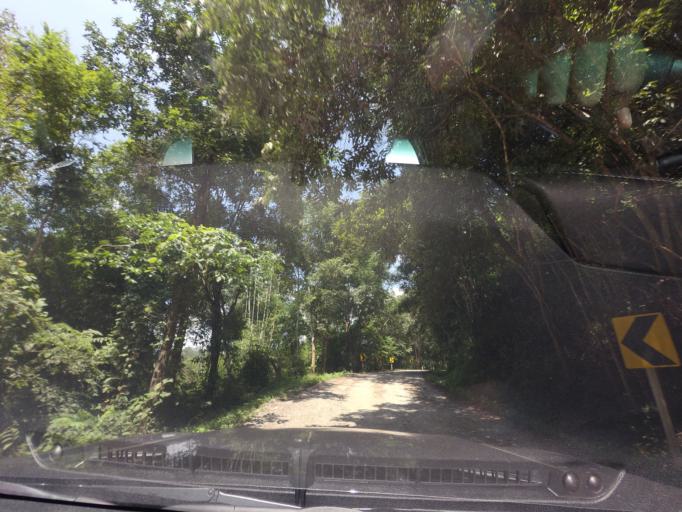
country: TH
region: Loei
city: Na Haeo
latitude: 17.6175
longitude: 100.8999
